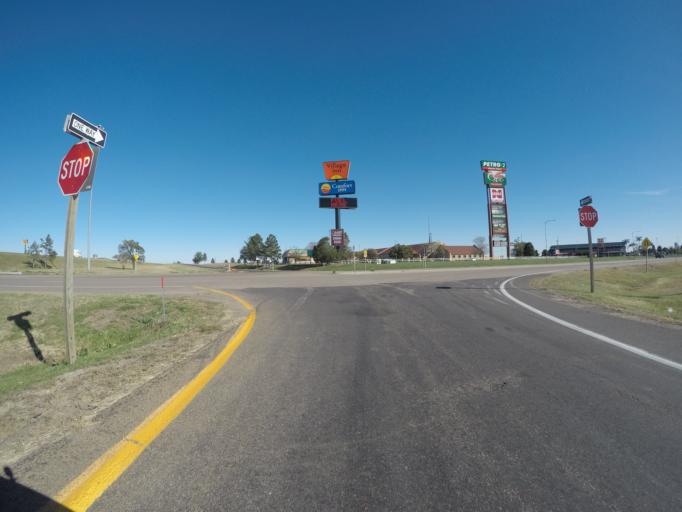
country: US
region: Kansas
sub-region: Thomas County
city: Colby
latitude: 39.3640
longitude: -101.0553
